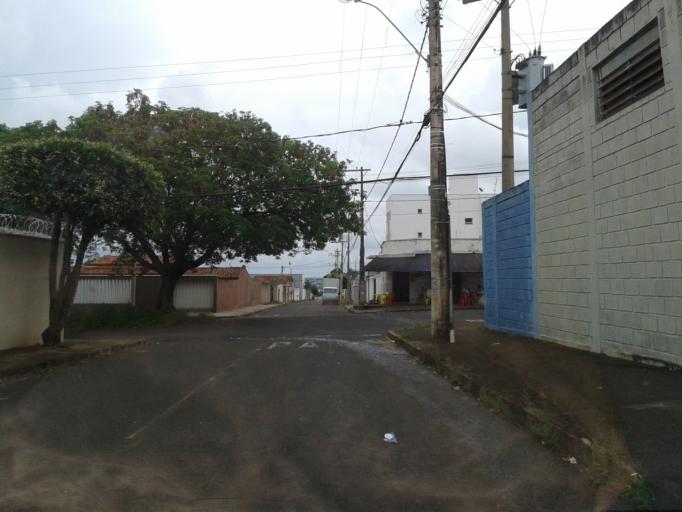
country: BR
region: Minas Gerais
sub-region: Uberlandia
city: Uberlandia
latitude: -18.9298
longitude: -48.2498
